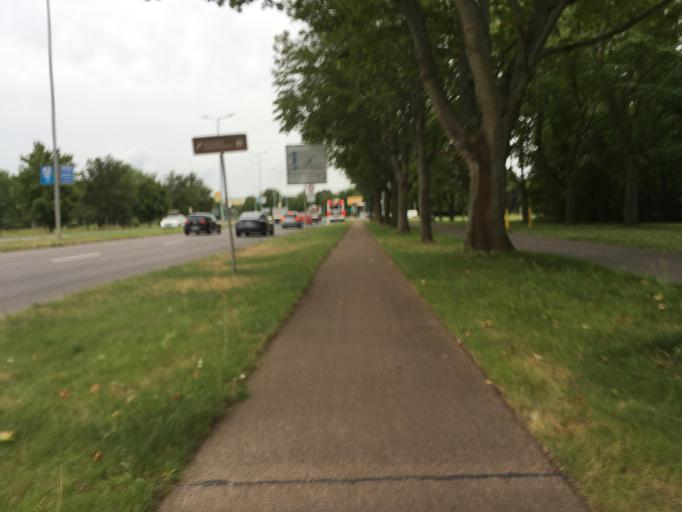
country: DE
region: Brandenburg
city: Schwedt (Oder)
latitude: 53.0642
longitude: 14.2712
